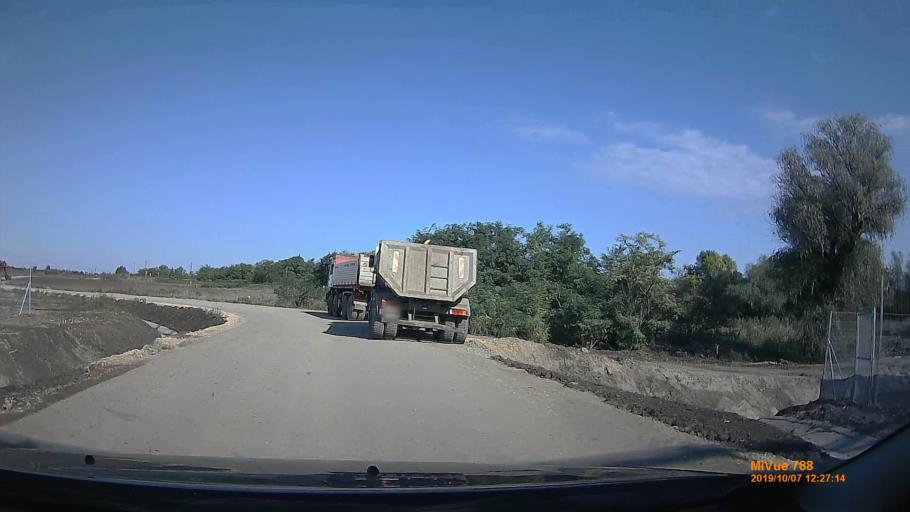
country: HU
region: Jasz-Nagykun-Szolnok
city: Kunszentmarton
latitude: 46.8692
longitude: 20.2730
